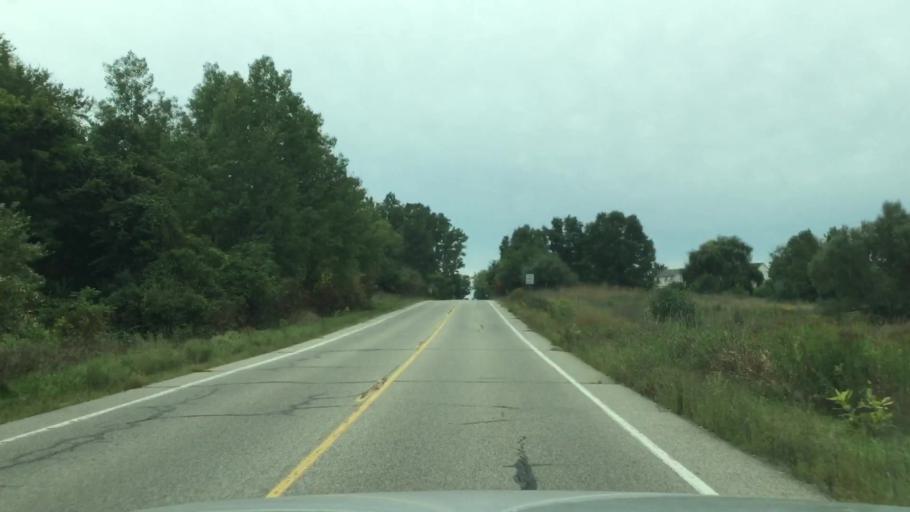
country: US
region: Michigan
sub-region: Washtenaw County
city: Ypsilanti
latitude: 42.2097
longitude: -83.6600
